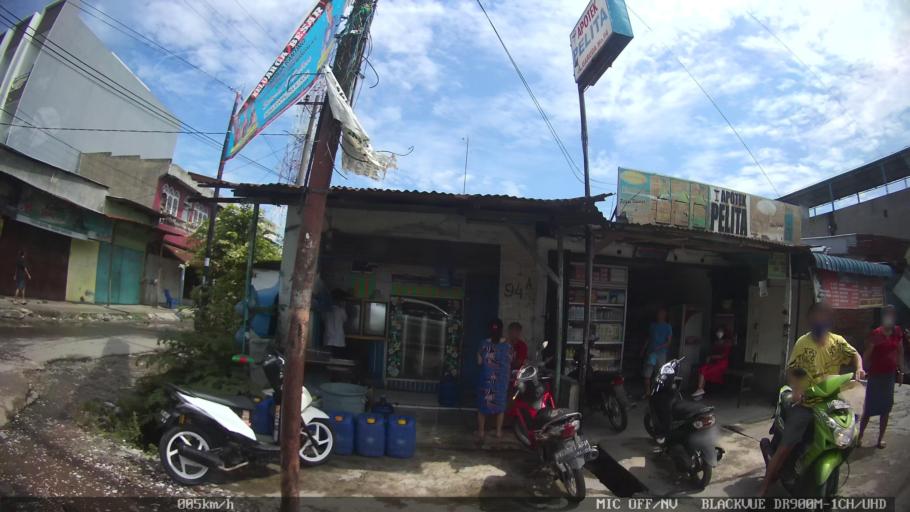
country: ID
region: North Sumatra
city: Medan
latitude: 3.5874
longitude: 98.7180
